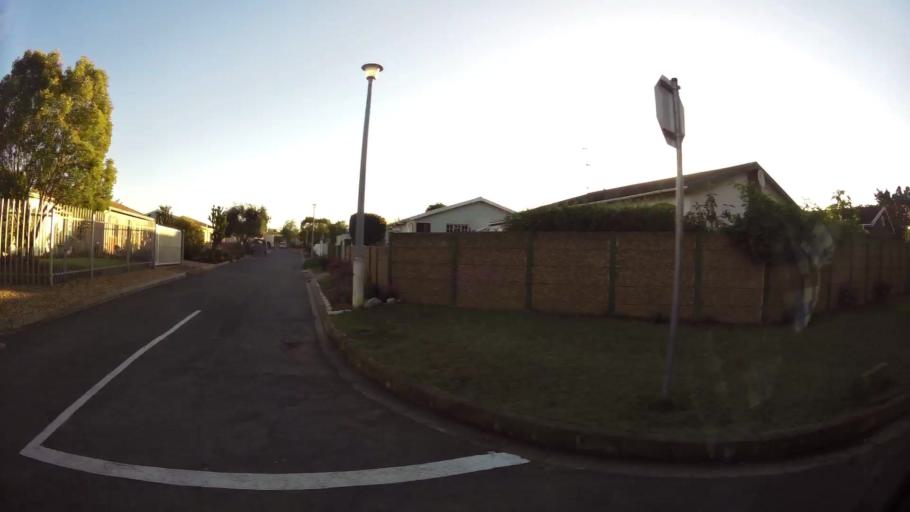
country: ZA
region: Western Cape
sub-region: Eden District Municipality
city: Riversdale
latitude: -34.0828
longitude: 21.2485
